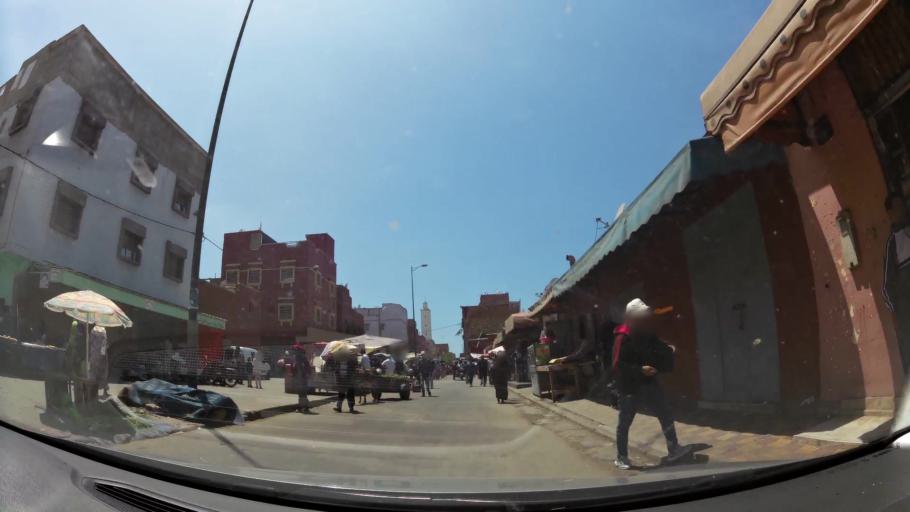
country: MA
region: Gharb-Chrarda-Beni Hssen
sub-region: Kenitra Province
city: Kenitra
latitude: 34.2567
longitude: -6.5576
